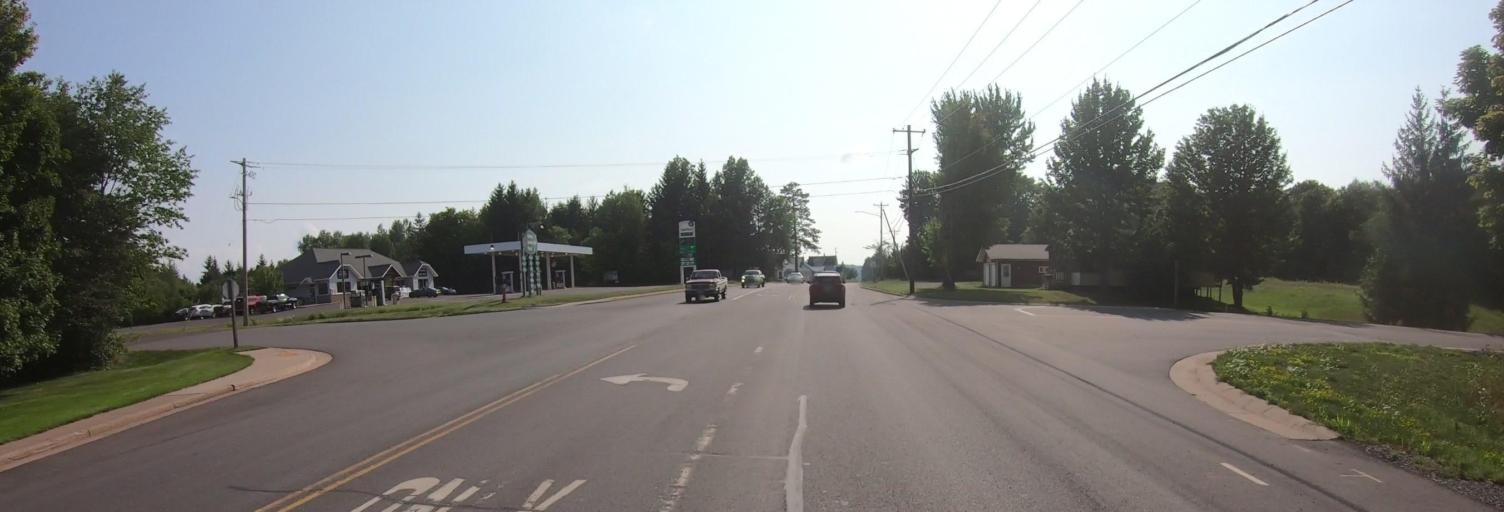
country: US
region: Wisconsin
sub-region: Iron County
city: Hurley
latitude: 46.4378
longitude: -90.2146
